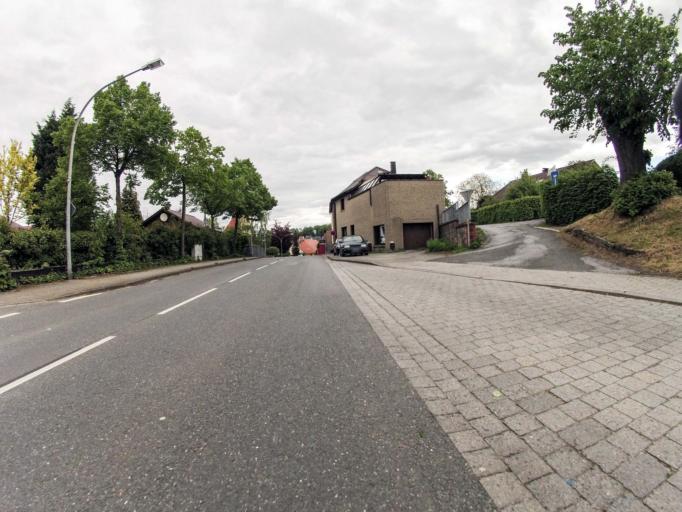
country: DE
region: Lower Saxony
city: Ostercappeln
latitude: 52.3425
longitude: 8.2226
